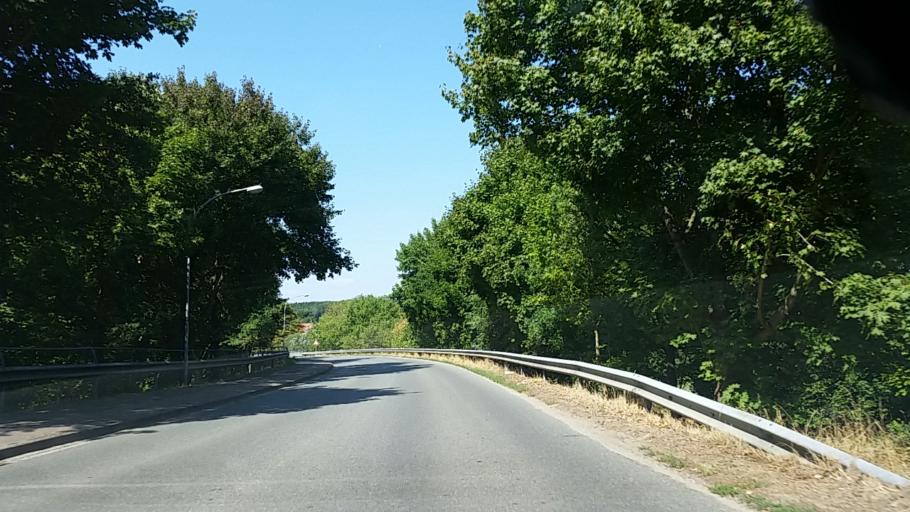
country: DE
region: Lower Saxony
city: Emmendorf
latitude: 53.0232
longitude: 10.5734
